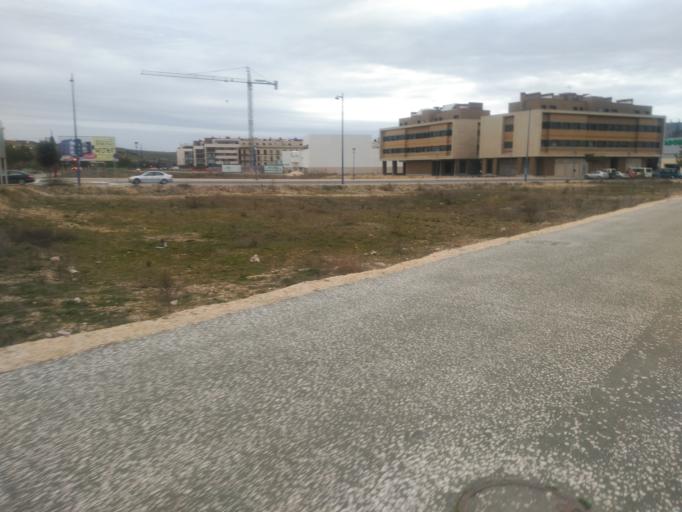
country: ES
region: Castille and Leon
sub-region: Provincia de Burgos
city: Burgos
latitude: 42.3335
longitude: -3.7103
